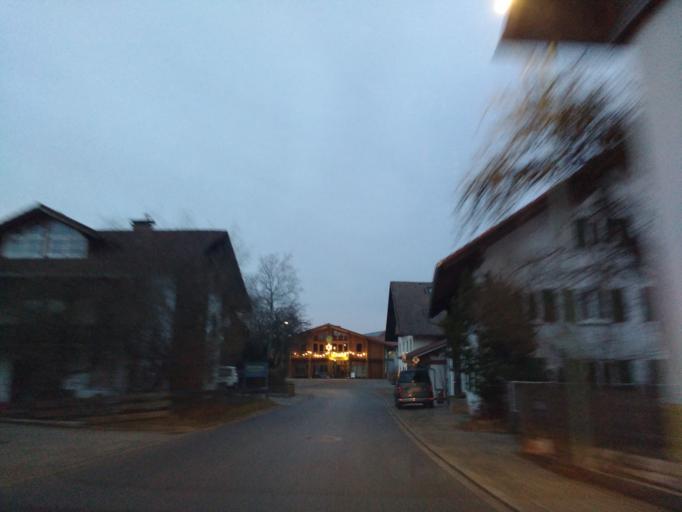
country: DE
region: Bavaria
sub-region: Upper Bavaria
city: Bernbeuren
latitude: 47.7731
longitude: 10.7495
